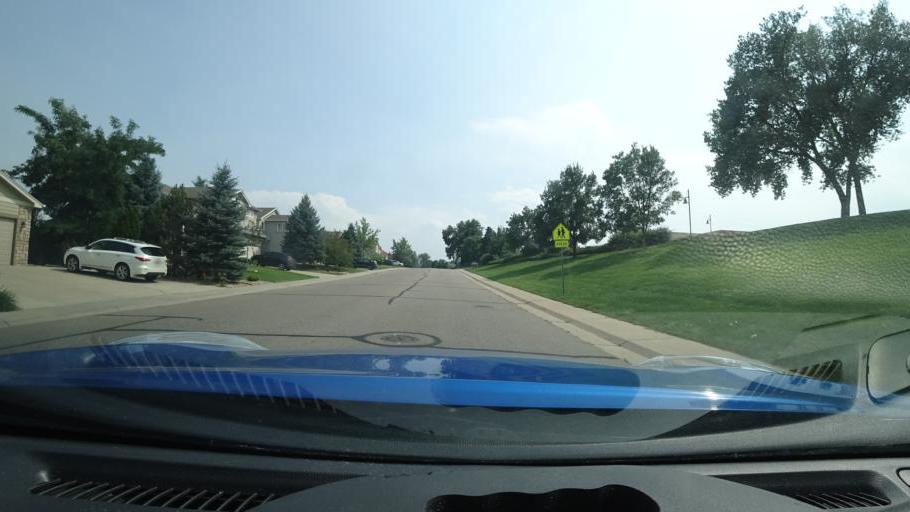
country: US
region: Colorado
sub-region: Adams County
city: Aurora
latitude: 39.6743
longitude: -104.8503
